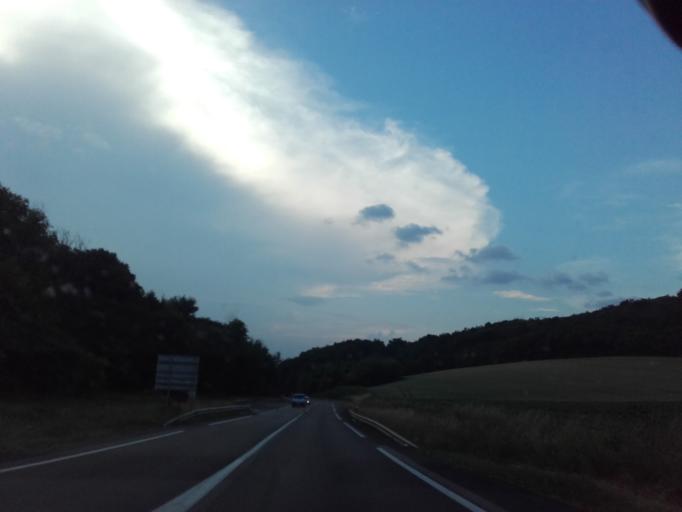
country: FR
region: Rhone-Alpes
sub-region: Departement de l'Isere
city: Chuzelles
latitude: 45.5907
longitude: 4.8602
